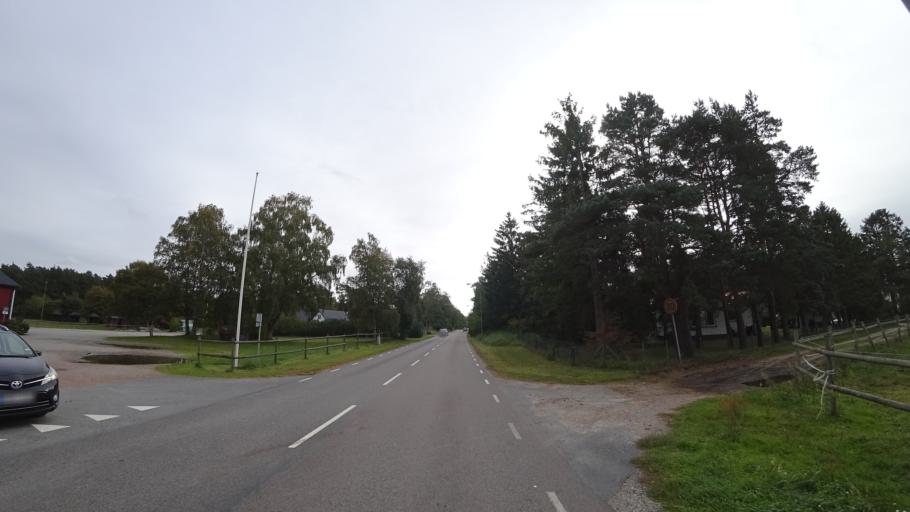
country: SE
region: Skane
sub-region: Kavlinge Kommun
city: Hofterup
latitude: 55.8027
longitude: 12.9858
